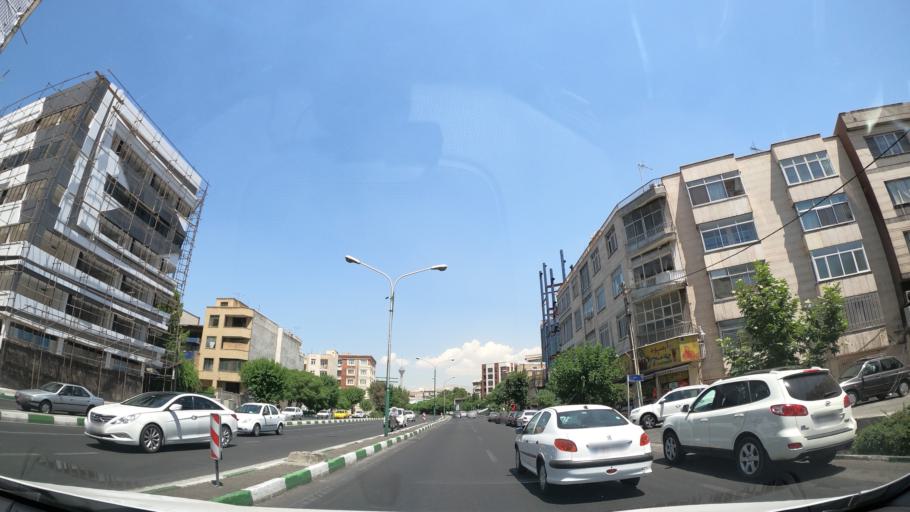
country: IR
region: Tehran
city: Tehran
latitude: 35.7228
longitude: 51.4004
